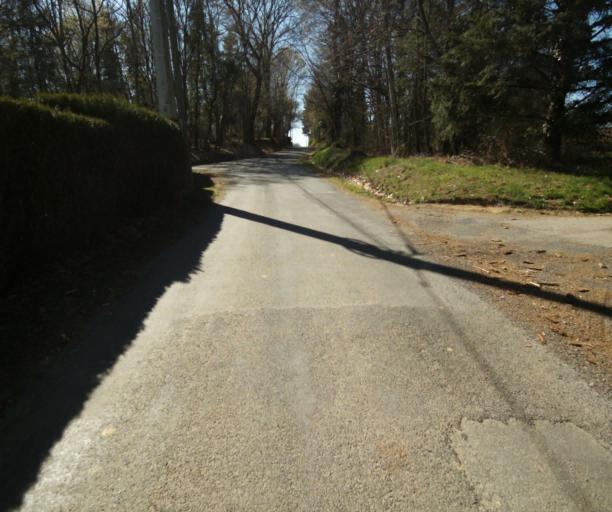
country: FR
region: Limousin
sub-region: Departement de la Correze
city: Chameyrat
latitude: 45.2536
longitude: 1.7066
